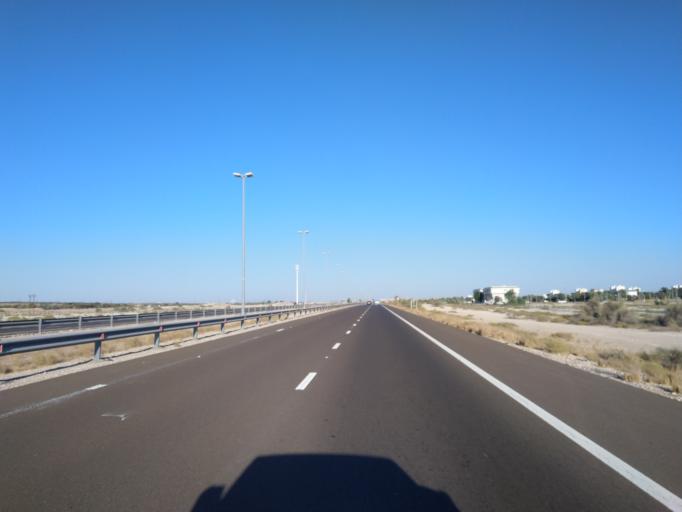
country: OM
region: Al Buraimi
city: Al Buraymi
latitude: 24.5222
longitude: 55.5332
